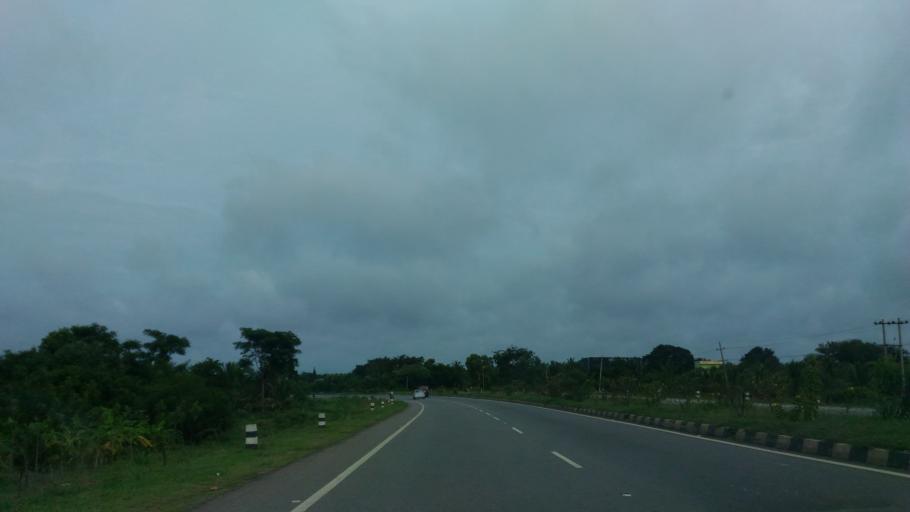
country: IN
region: Karnataka
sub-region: Tumkur
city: Kunigal
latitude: 13.0418
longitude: 77.1174
